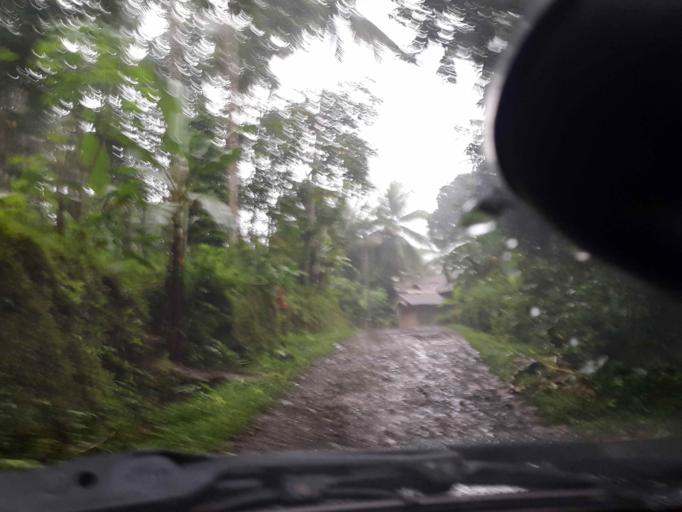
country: ID
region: Central Java
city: Kutoarjo
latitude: -7.5607
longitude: 109.9736
